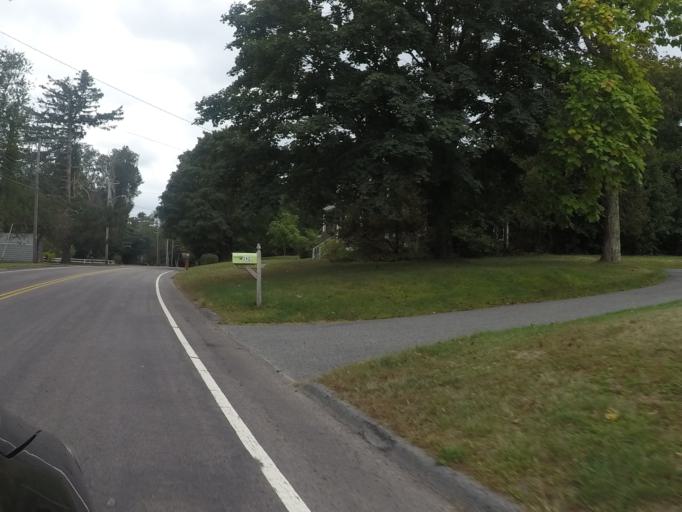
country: US
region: Massachusetts
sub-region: Bristol County
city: Smith Mills
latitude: 41.6190
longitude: -70.9988
